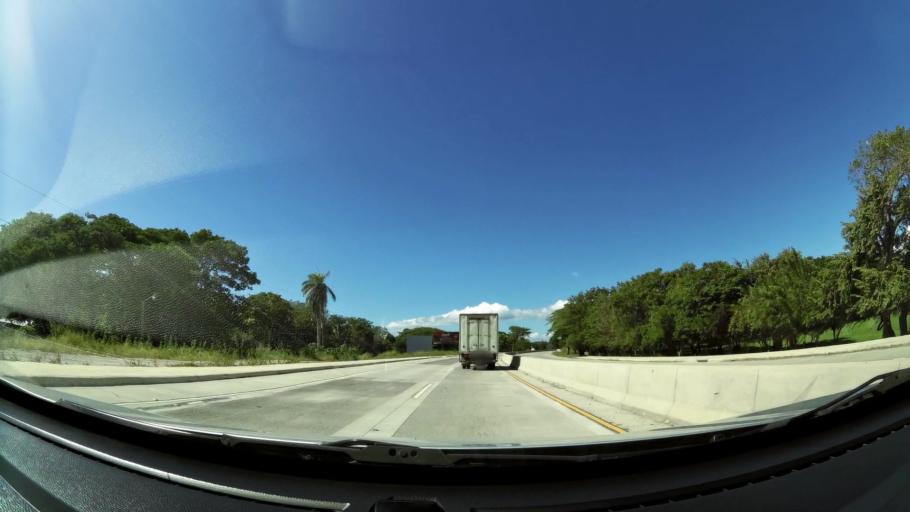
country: CR
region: Guanacaste
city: Liberia
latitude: 10.5885
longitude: -85.4185
